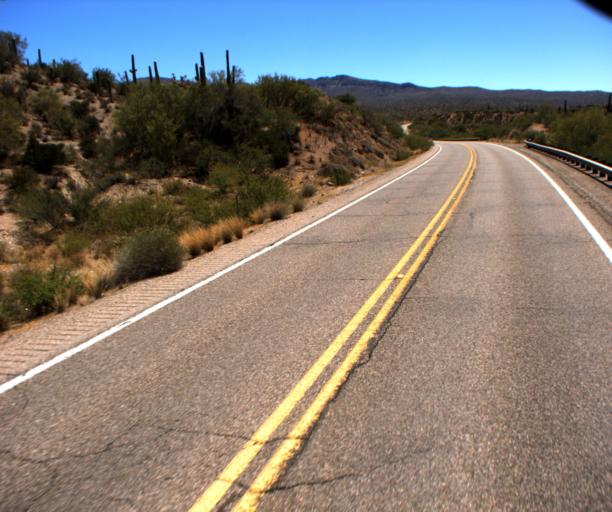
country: US
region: Arizona
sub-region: Pinal County
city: Kearny
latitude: 33.1174
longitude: -110.9693
